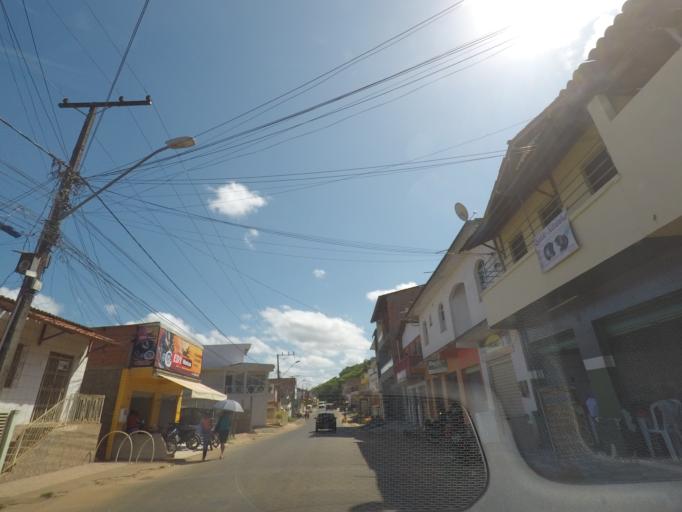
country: BR
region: Bahia
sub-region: Itubera
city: Itubera
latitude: -13.7408
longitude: -39.1502
